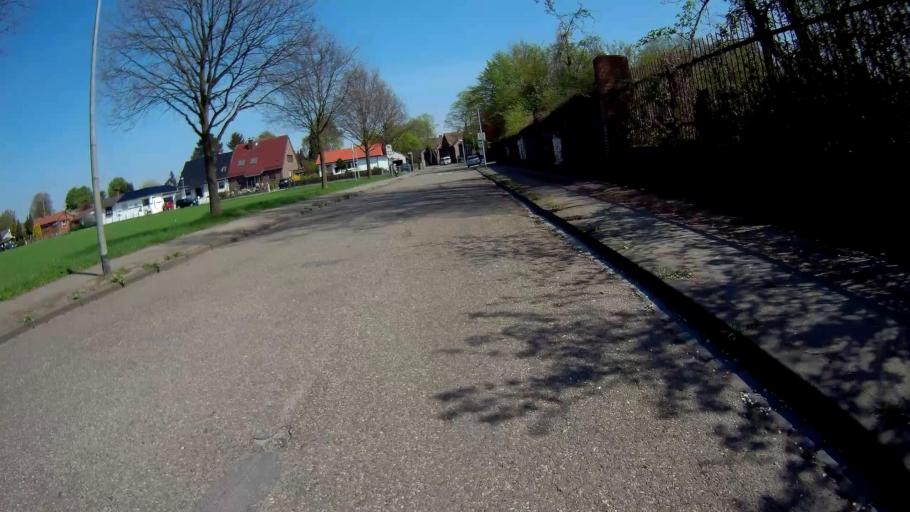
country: DE
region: North Rhine-Westphalia
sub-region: Regierungsbezirk Munster
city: Gladbeck
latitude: 51.5470
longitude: 7.0512
